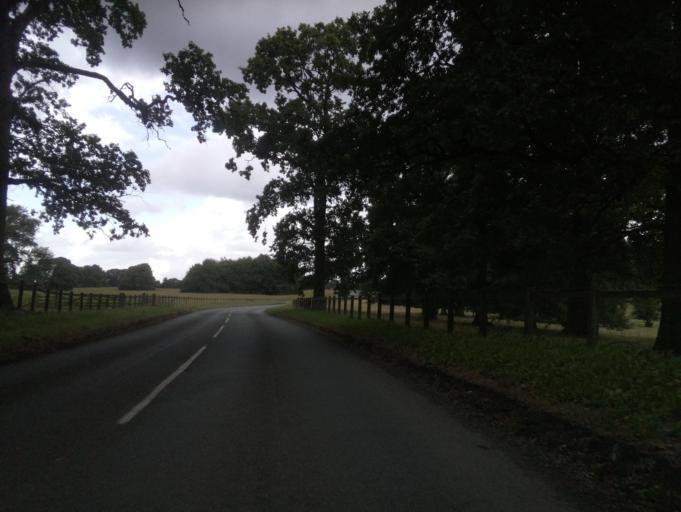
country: GB
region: England
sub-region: Staffordshire
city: Eccleshall
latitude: 52.9102
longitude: -2.2219
